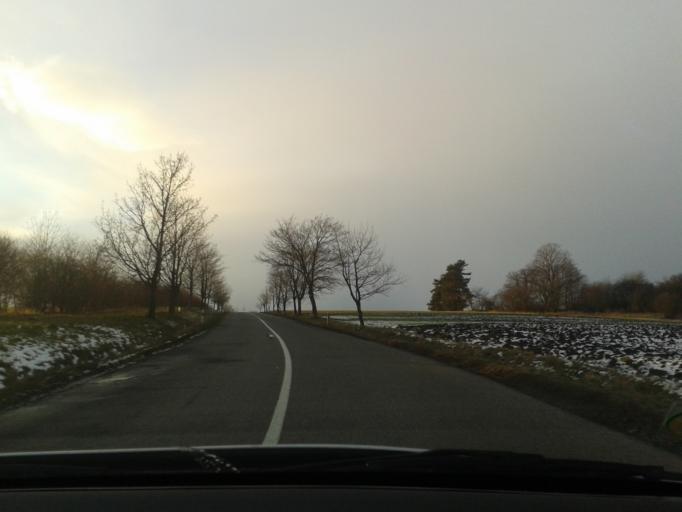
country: CZ
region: Olomoucky
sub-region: Okres Prostejov
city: Plumlov
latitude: 49.4895
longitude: 17.0137
